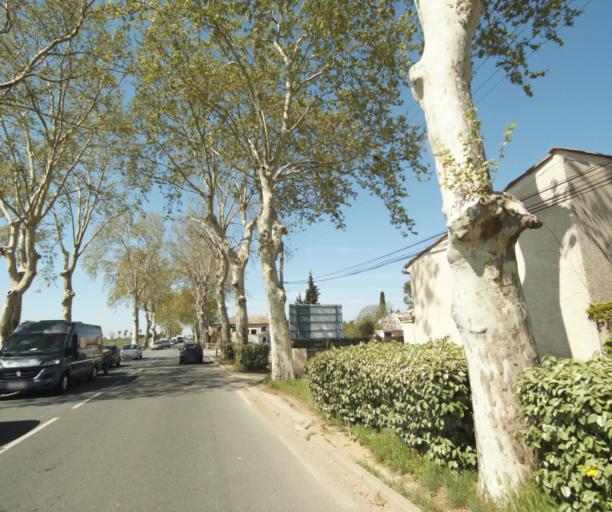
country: FR
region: Languedoc-Roussillon
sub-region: Departement de l'Herault
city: Baillargues
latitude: 43.6563
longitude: 4.0060
